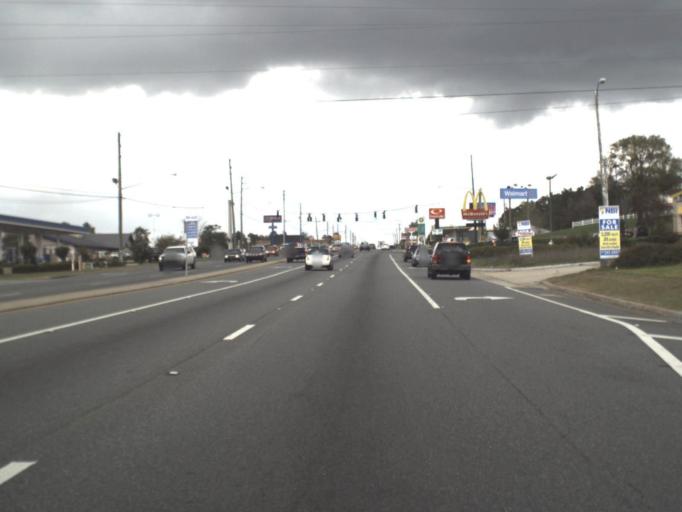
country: US
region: Florida
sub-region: Okaloosa County
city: Crestview
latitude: 30.7276
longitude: -86.5681
